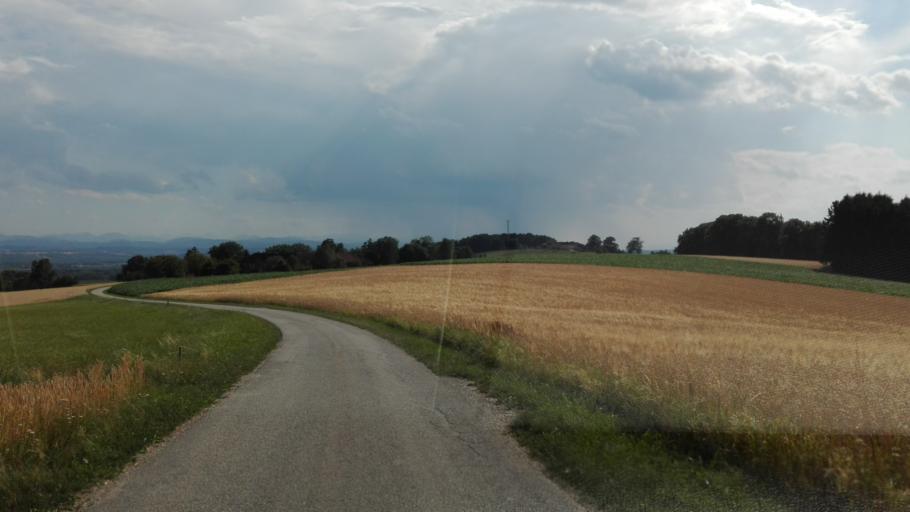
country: AT
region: Upper Austria
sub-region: Politischer Bezirk Perg
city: Bad Kreuzen
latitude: 48.2385
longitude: 14.7226
